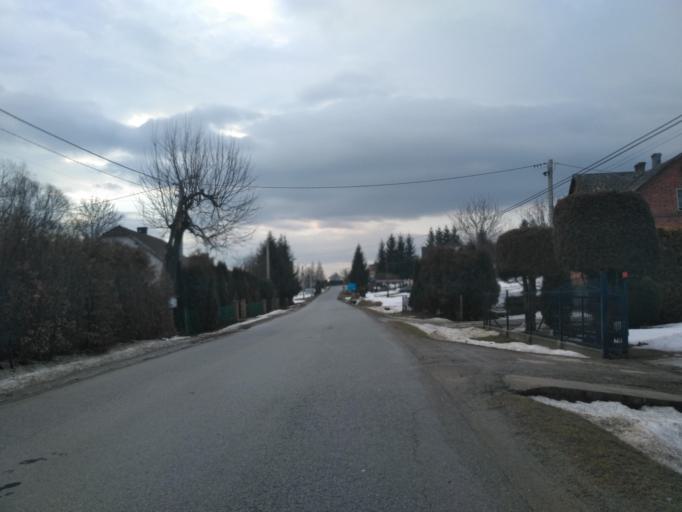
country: PL
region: Subcarpathian Voivodeship
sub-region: Powiat brzozowski
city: Dydnia
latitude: 49.6291
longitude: 22.1608
